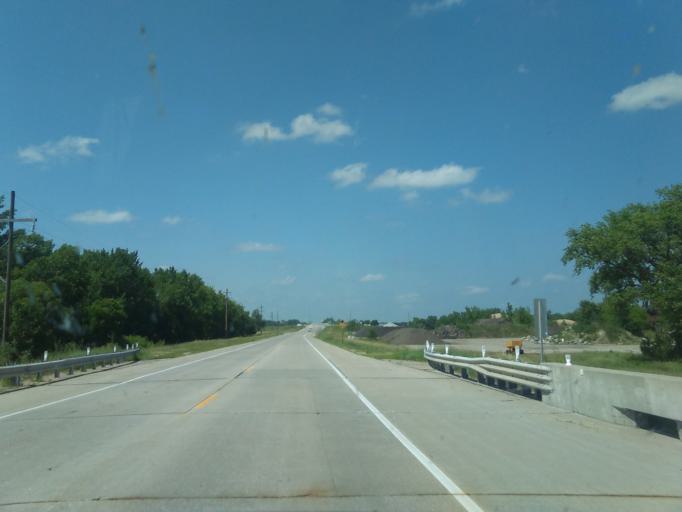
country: US
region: Nebraska
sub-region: Phelps County
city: Holdrege
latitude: 40.6832
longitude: -99.3802
